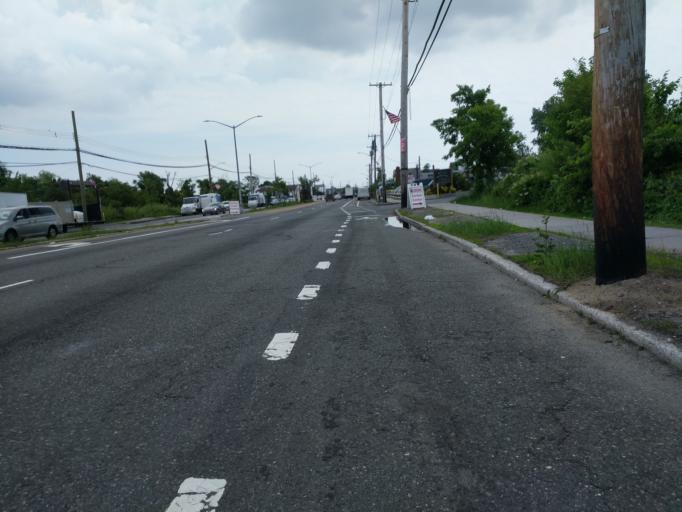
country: US
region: New York
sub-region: Queens County
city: Borough of Queens
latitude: 40.6149
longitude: -73.8219
